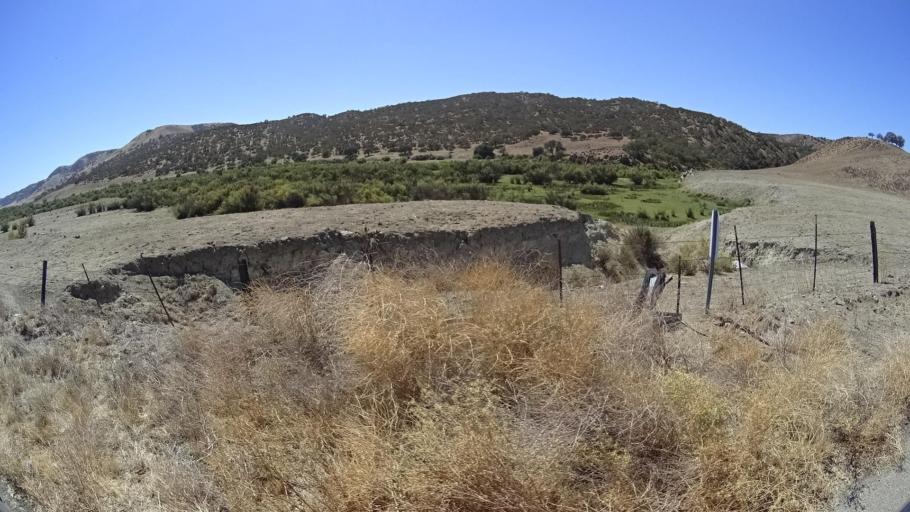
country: US
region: California
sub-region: Monterey County
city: King City
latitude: 36.2927
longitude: -120.9738
